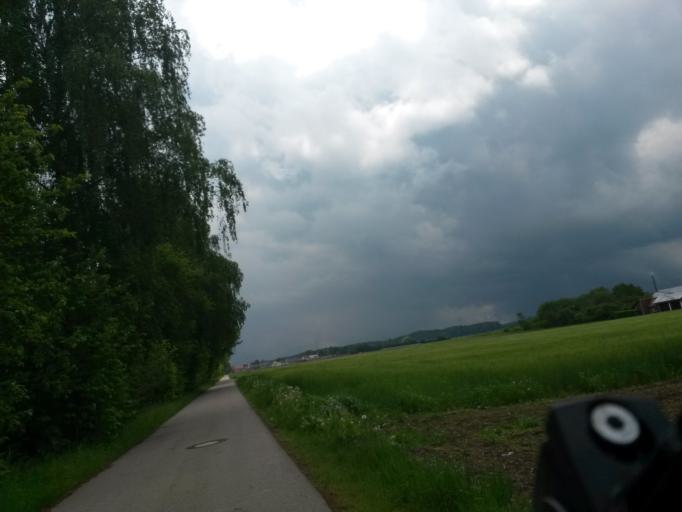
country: DE
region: Baden-Wuerttemberg
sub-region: Tuebingen Region
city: Bad Waldsee
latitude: 47.9317
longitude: 9.8086
